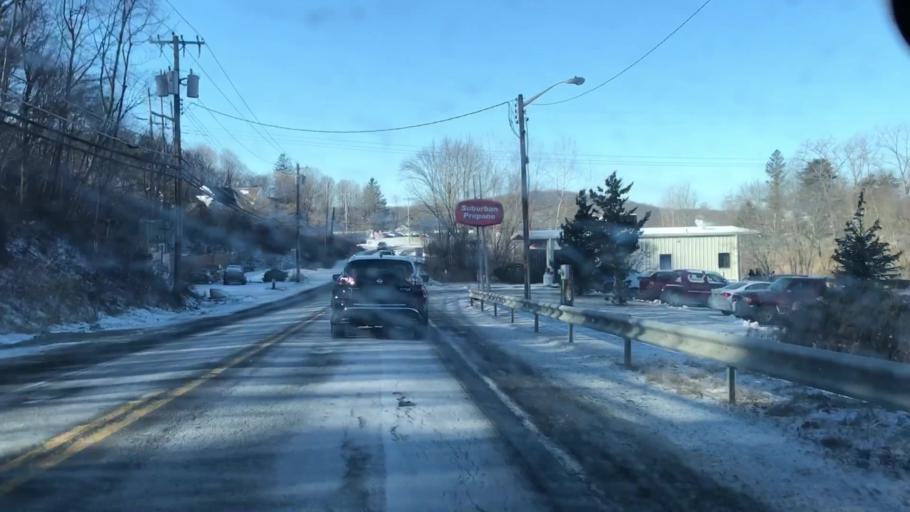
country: US
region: New York
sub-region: Putnam County
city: Brewster
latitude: 41.3993
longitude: -73.6298
